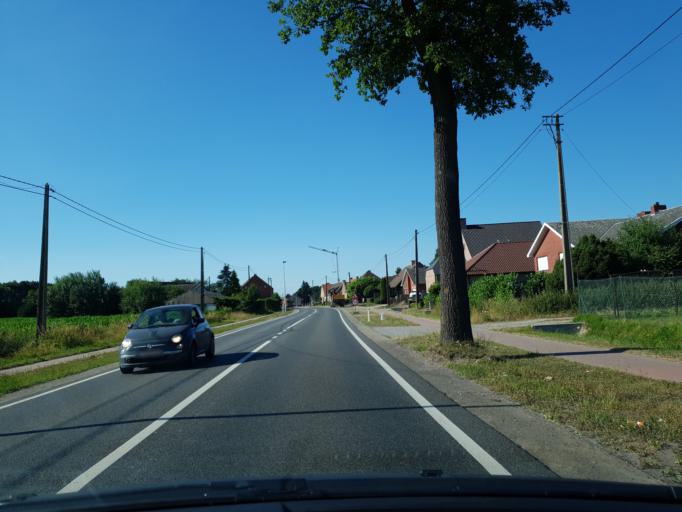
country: BE
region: Flanders
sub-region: Provincie Antwerpen
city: Rijkevorsel
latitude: 51.3630
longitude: 4.7585
